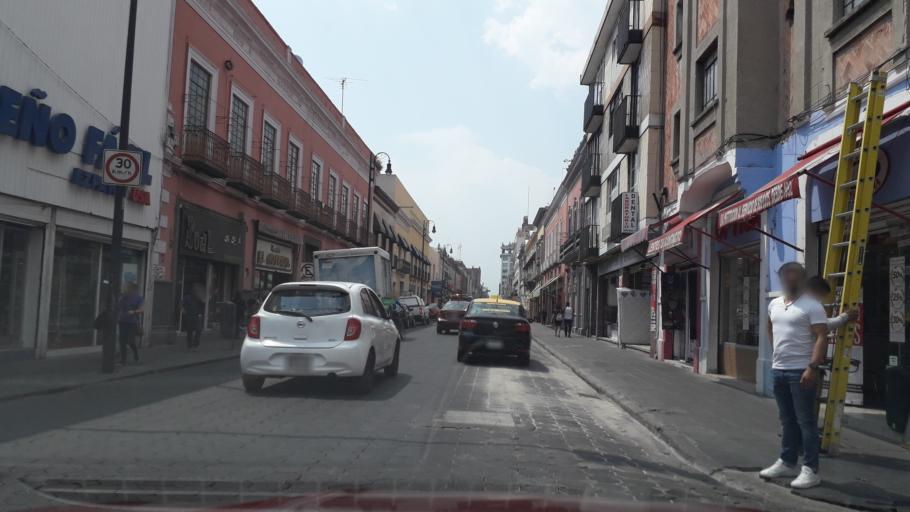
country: MX
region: Puebla
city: Puebla
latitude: 19.0468
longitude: -98.2012
